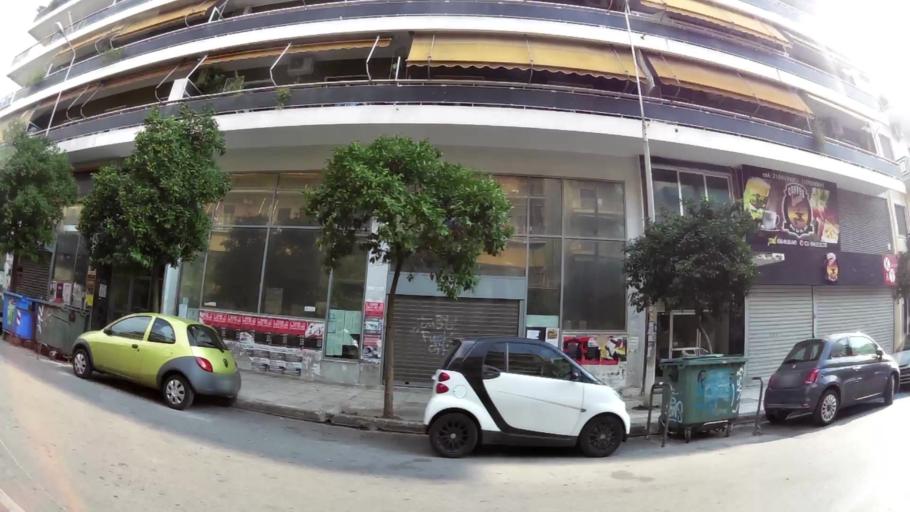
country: GR
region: Attica
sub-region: Nomarchia Athinas
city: Kallithea
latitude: 37.9533
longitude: 23.7062
